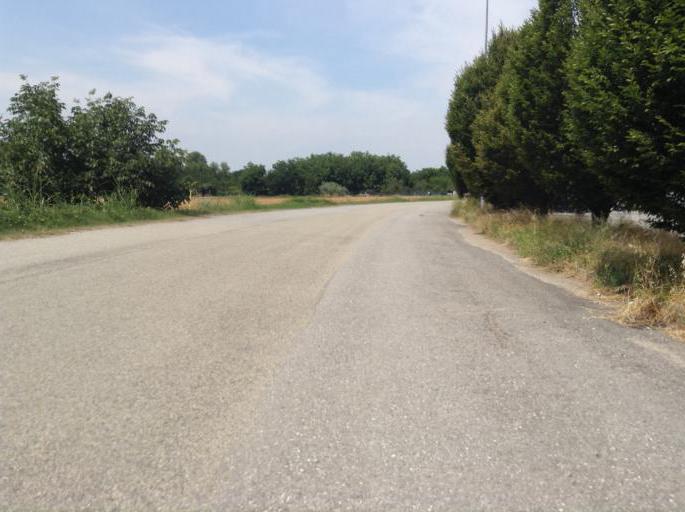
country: IT
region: Piedmont
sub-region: Provincia di Torino
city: Carignano
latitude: 44.8953
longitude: 7.6671
